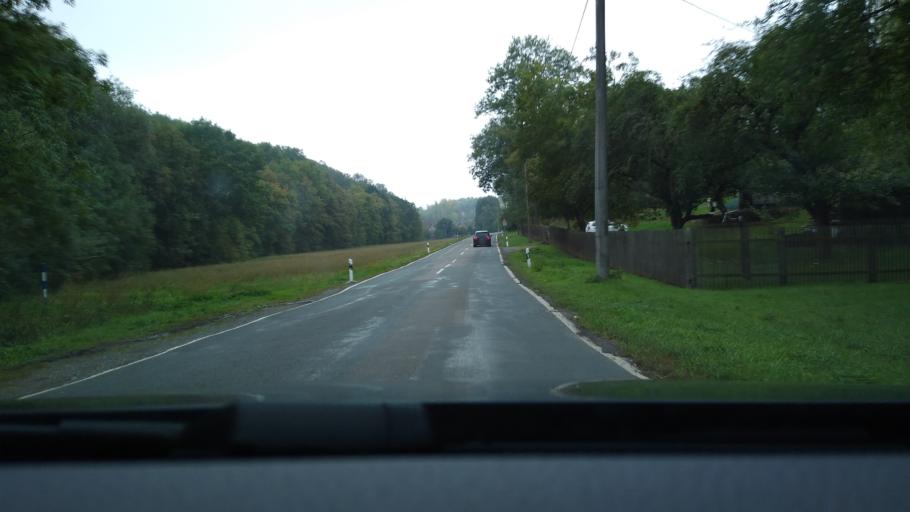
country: DE
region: Saxony-Anhalt
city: Polleben
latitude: 51.6002
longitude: 11.6122
